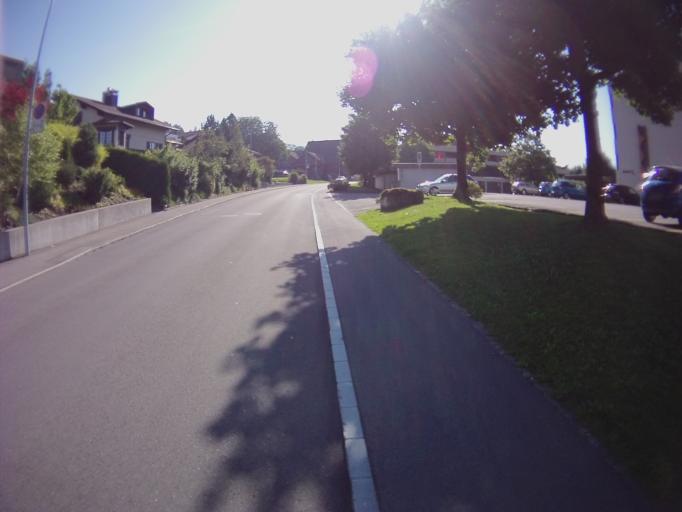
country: CH
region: Zug
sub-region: Zug
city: Unterageri
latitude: 47.1373
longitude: 8.6070
